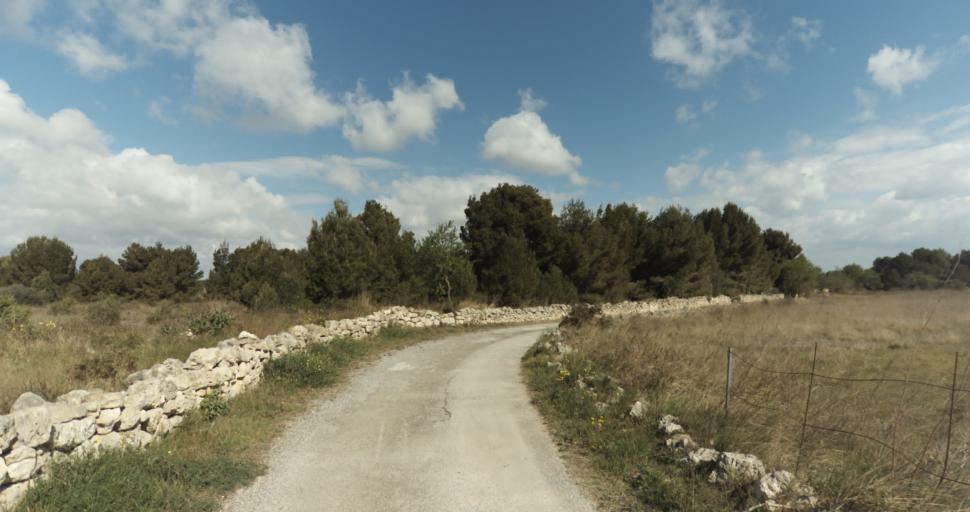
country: FR
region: Languedoc-Roussillon
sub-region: Departement de l'Aude
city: Leucate
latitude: 42.9267
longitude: 3.0375
